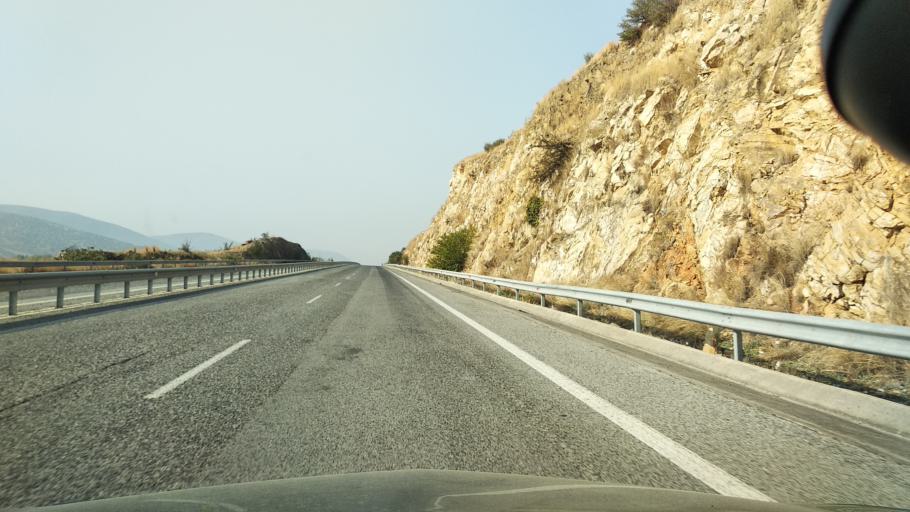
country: GR
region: Thessaly
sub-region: Trikala
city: Zarkos
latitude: 39.5937
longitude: 22.1757
